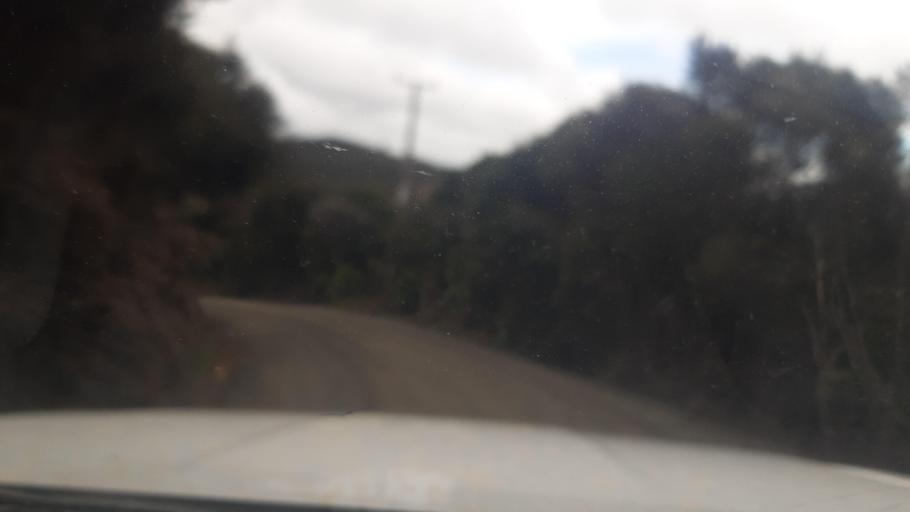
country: NZ
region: Northland
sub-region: Far North District
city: Taipa
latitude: -35.0603
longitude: 173.5327
